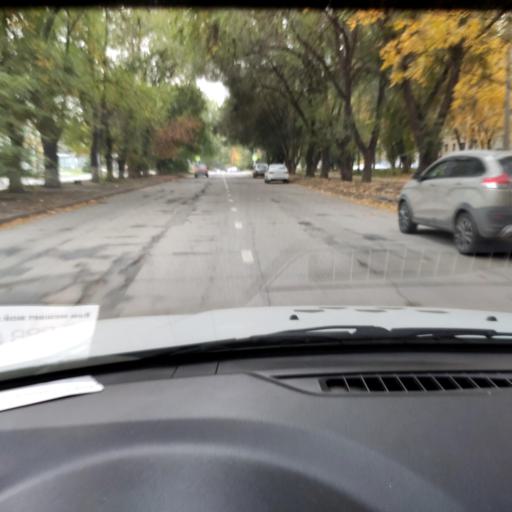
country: RU
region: Samara
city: Tol'yatti
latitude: 53.5216
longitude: 49.4303
